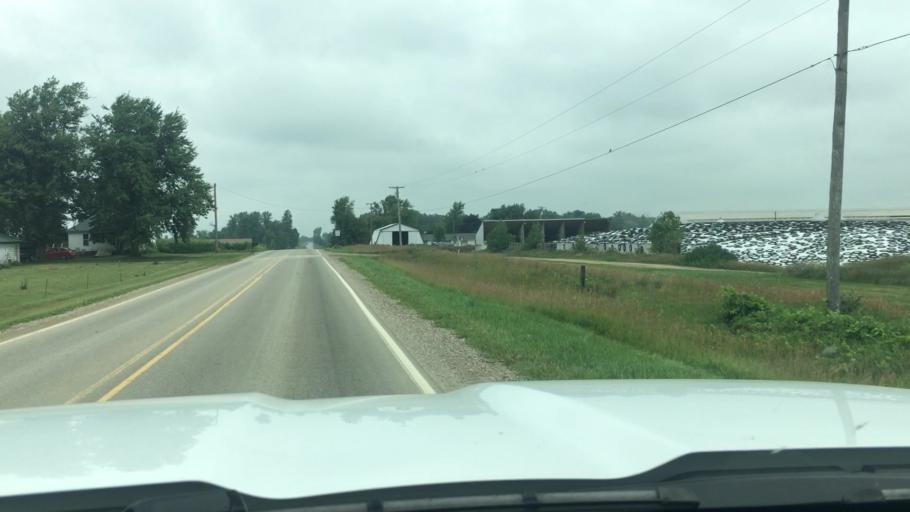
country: US
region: Michigan
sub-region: Sanilac County
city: Marlette
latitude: 43.3115
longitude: -82.9837
